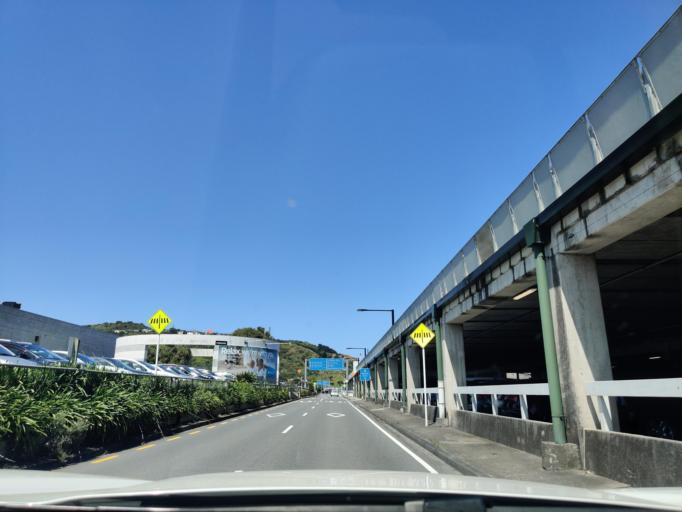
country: NZ
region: Wellington
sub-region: Wellington City
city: Wellington
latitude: -41.3287
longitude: 174.8130
